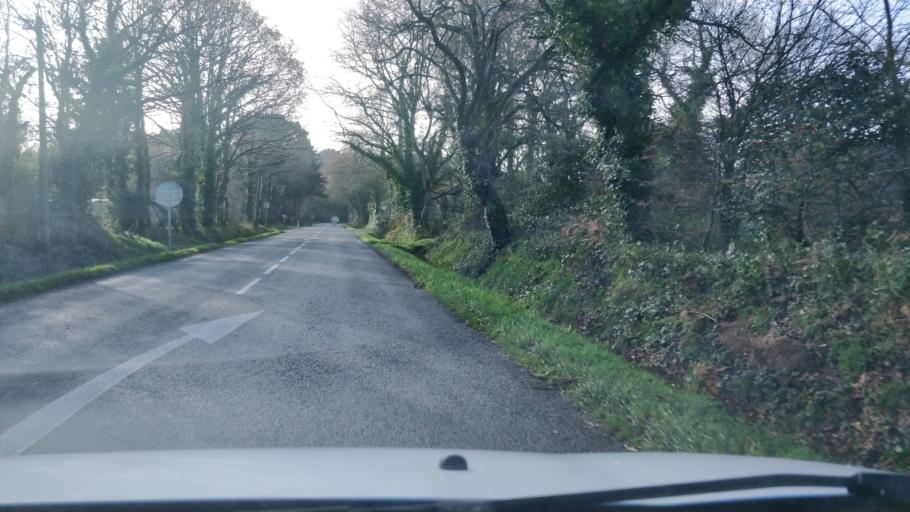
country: FR
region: Pays de la Loire
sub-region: Departement de la Loire-Atlantique
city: Saint-Molf
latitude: 47.3744
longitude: -2.4328
